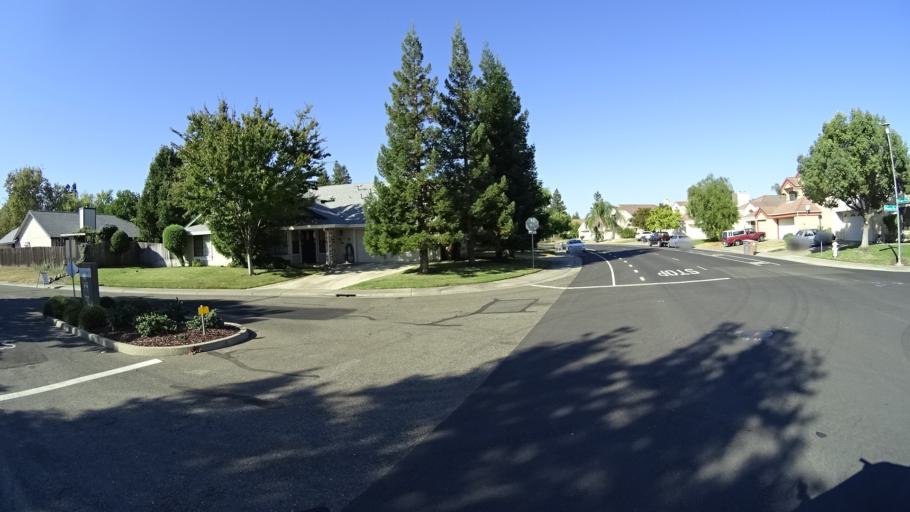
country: US
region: California
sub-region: Sacramento County
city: Laguna
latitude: 38.4302
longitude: -121.4415
